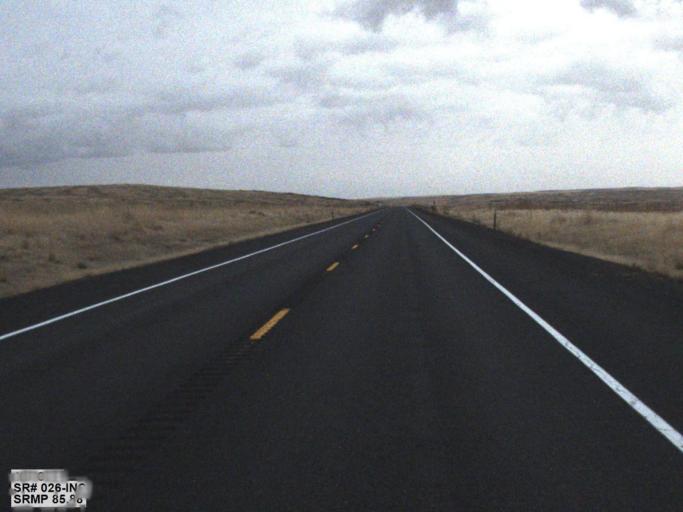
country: US
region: Washington
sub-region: Adams County
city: Ritzville
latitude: 46.7475
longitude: -118.2520
